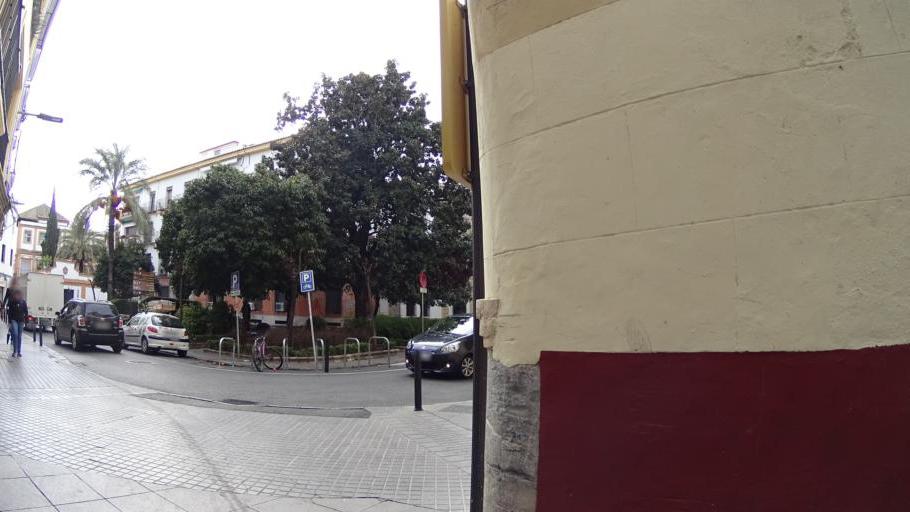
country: ES
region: Andalusia
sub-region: Province of Cordoba
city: Cordoba
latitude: 37.8834
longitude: -4.7821
